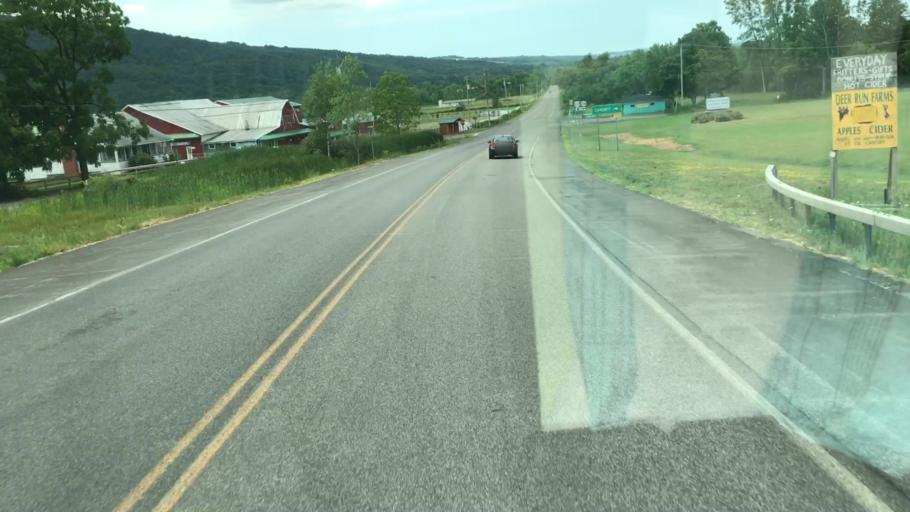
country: US
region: New York
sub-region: Onondaga County
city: Nedrow
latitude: 42.8921
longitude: -76.1475
